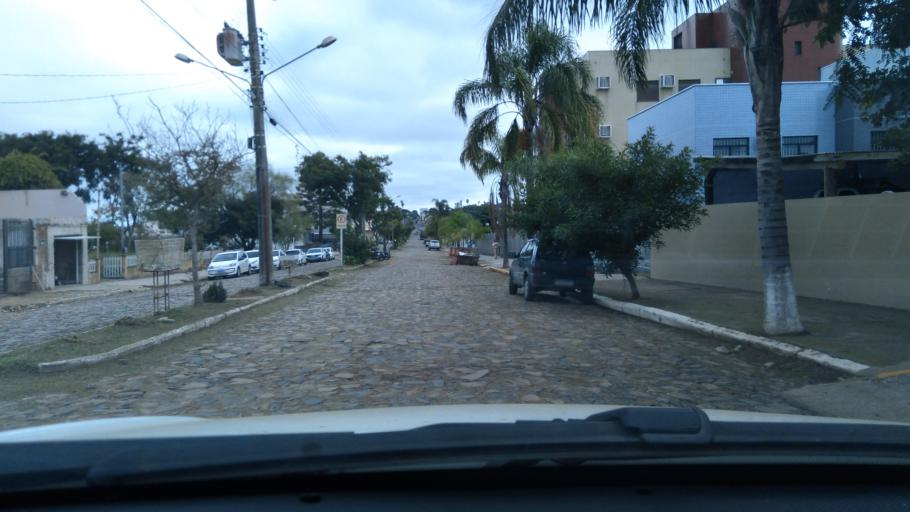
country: BR
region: Rio Grande do Sul
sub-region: Dom Pedrito
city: Dom Pedrito
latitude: -30.9863
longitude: -54.6652
